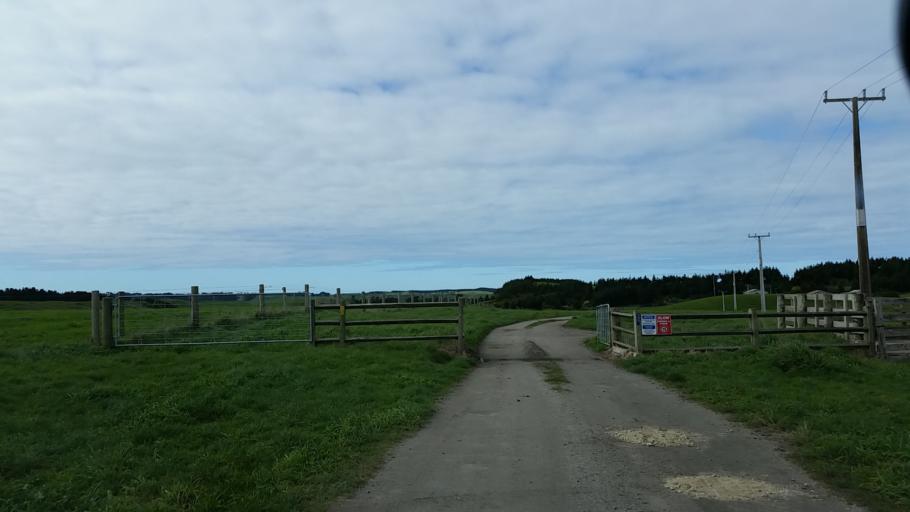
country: NZ
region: Taranaki
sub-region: South Taranaki District
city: Patea
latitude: -39.8079
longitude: 174.6996
